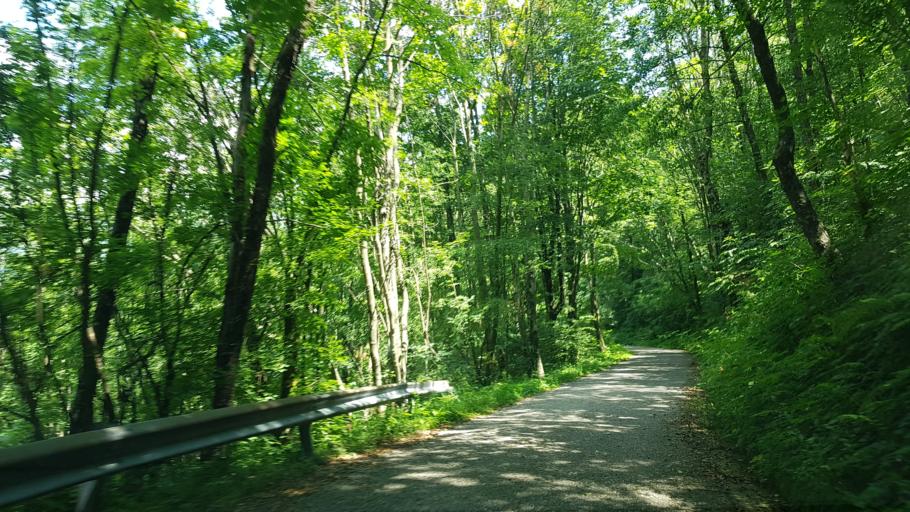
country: IT
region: Friuli Venezia Giulia
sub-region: Provincia di Udine
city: Lusevera
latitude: 46.2515
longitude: 13.2769
